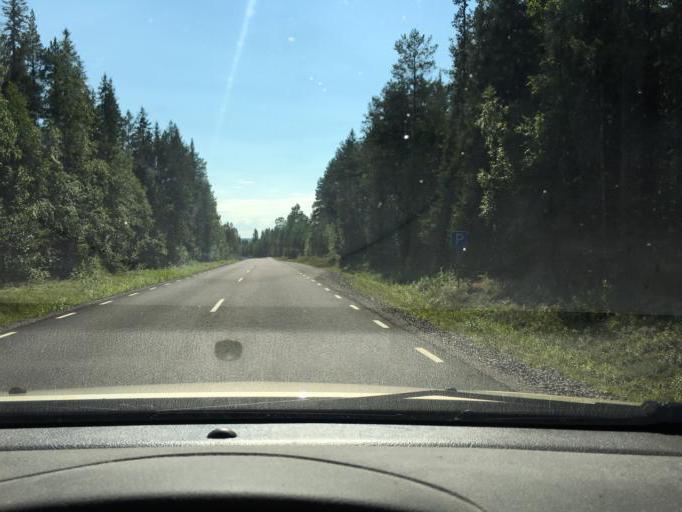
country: SE
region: Norrbotten
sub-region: Lulea Kommun
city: Ranea
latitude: 66.0432
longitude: 22.1879
